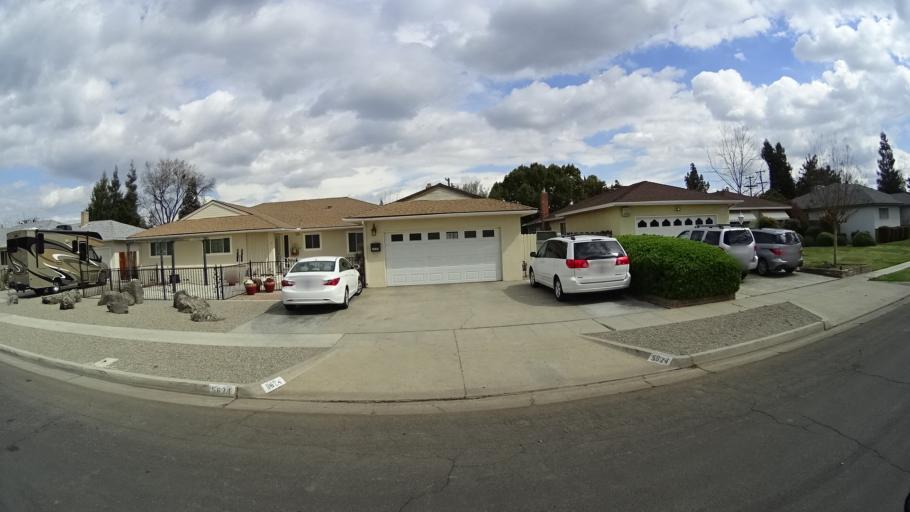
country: US
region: California
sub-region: Fresno County
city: Clovis
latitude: 36.8198
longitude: -119.7673
